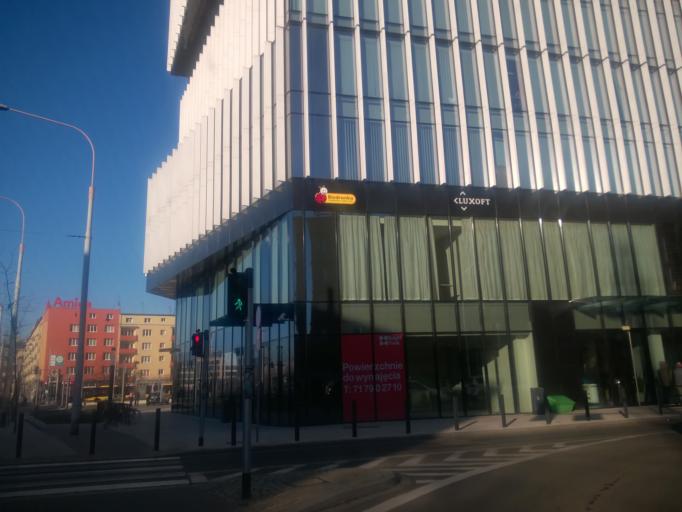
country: PL
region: Lower Silesian Voivodeship
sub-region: Powiat wroclawski
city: Wroclaw
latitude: 51.0992
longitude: 17.0403
